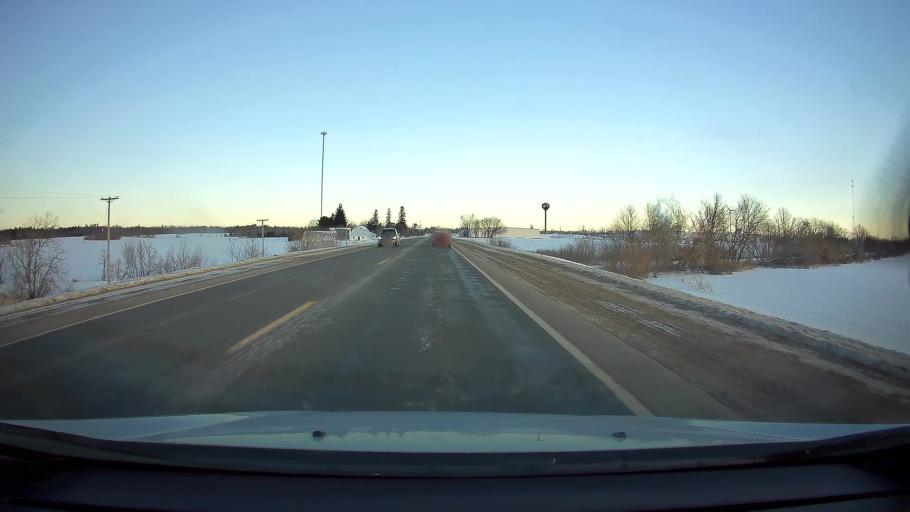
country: US
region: Wisconsin
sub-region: Barron County
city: Turtle Lake
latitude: 45.3846
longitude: -92.1666
